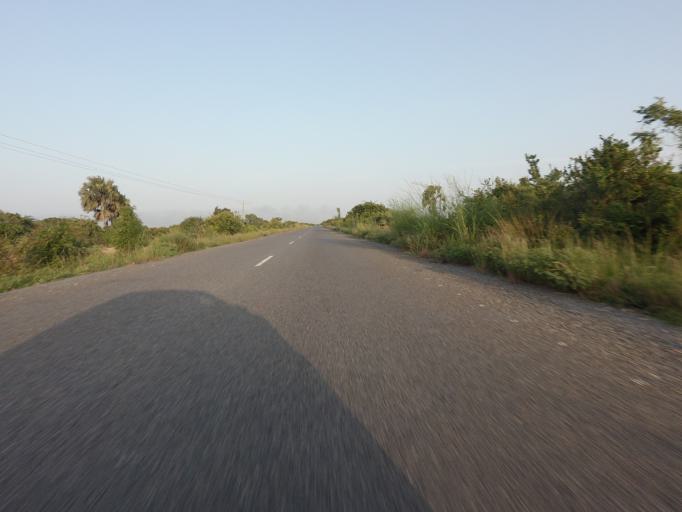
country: GH
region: Volta
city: Anloga
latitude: 5.8510
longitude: 0.7732
